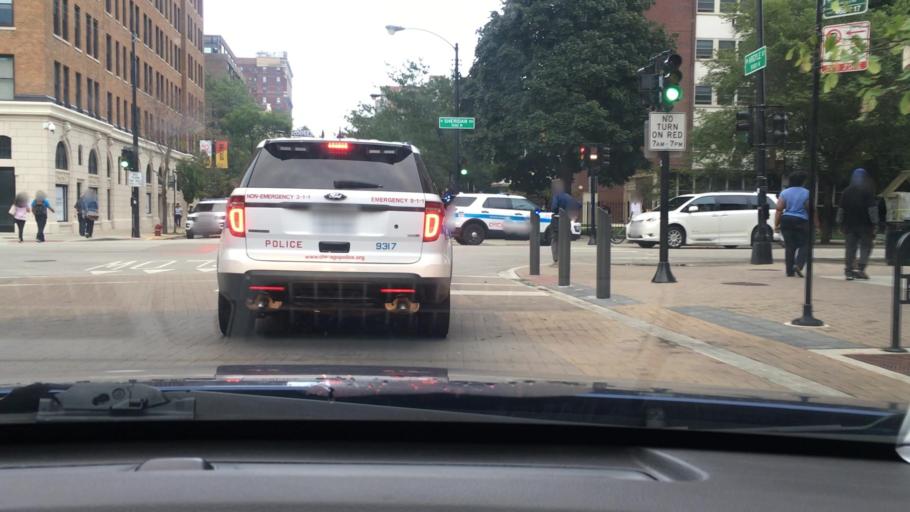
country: US
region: Illinois
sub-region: Cook County
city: Evanston
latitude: 41.9733
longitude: -87.6552
